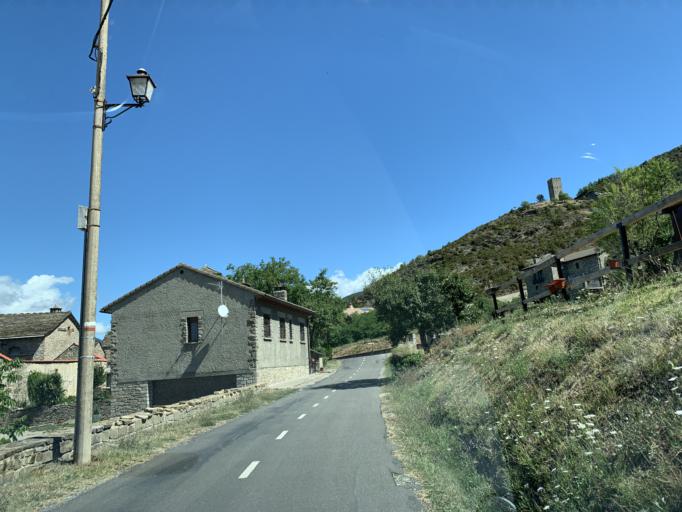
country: ES
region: Aragon
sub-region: Provincia de Huesca
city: Sabinanigo
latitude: 42.5536
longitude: -0.3180
